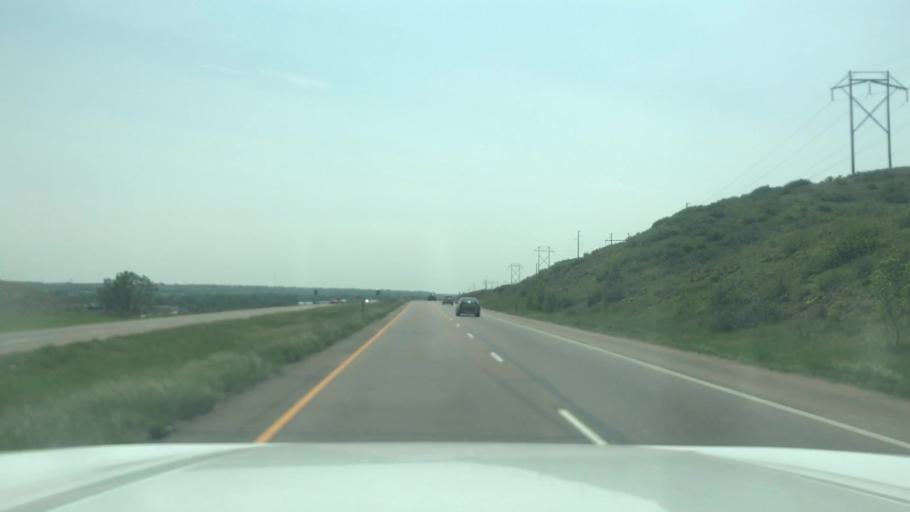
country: US
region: Colorado
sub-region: El Paso County
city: Security-Widefield
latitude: 38.7344
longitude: -104.7428
